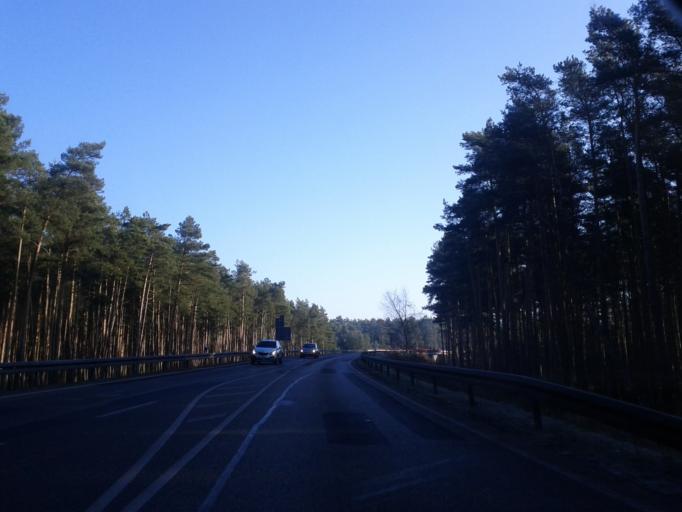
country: DE
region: Brandenburg
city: Grunheide
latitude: 52.3919
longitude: 13.7994
